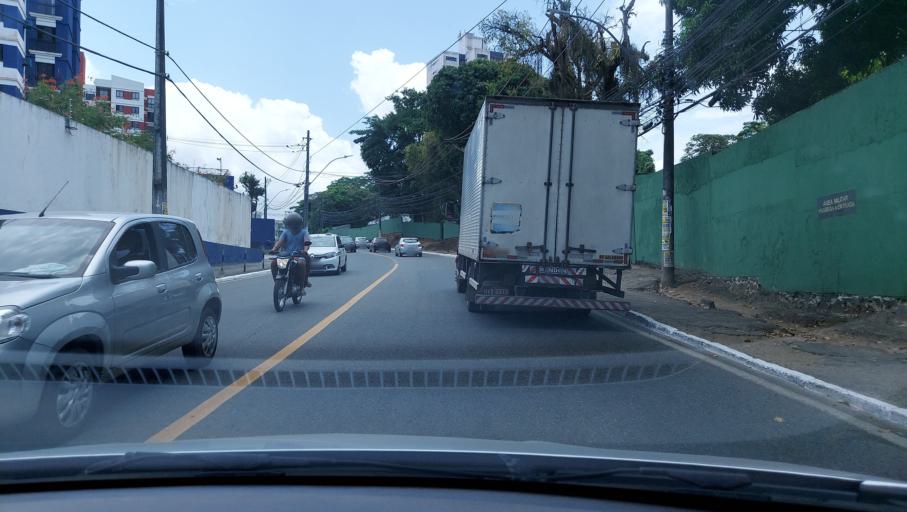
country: BR
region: Bahia
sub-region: Salvador
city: Salvador
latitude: -12.9566
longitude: -38.4644
